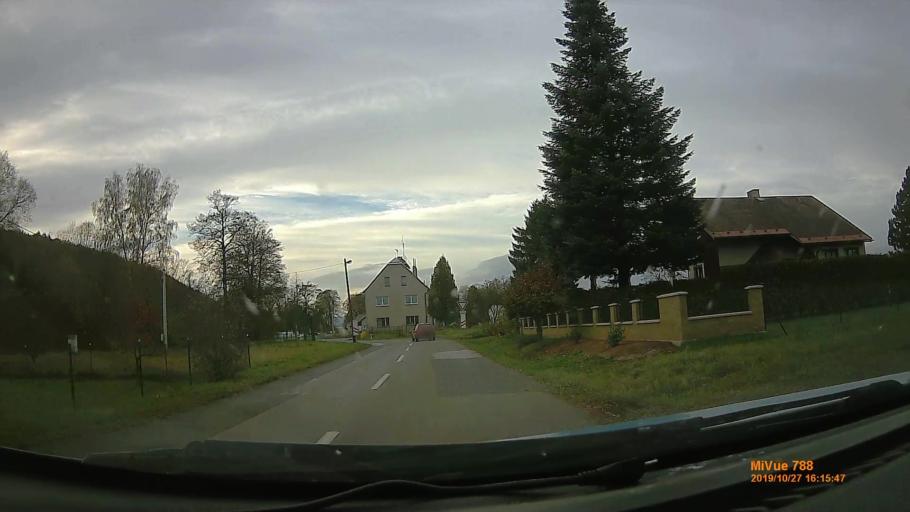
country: CZ
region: Kralovehradecky
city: Broumov
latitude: 50.5595
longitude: 16.3803
